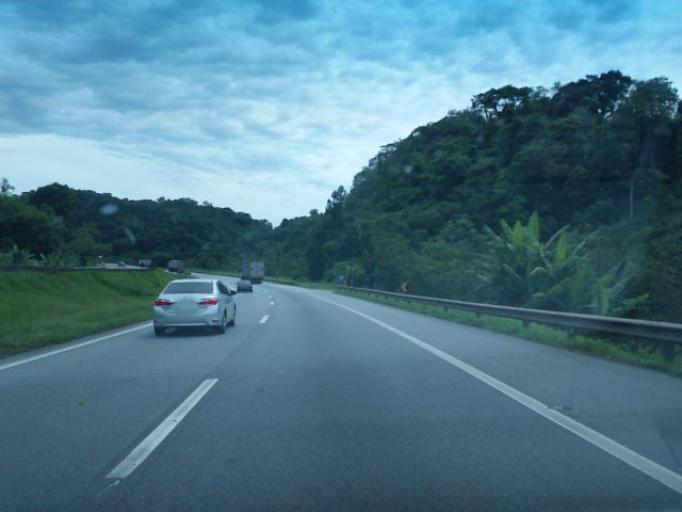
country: BR
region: Sao Paulo
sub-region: Miracatu
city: Miracatu
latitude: -24.1849
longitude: -47.3588
